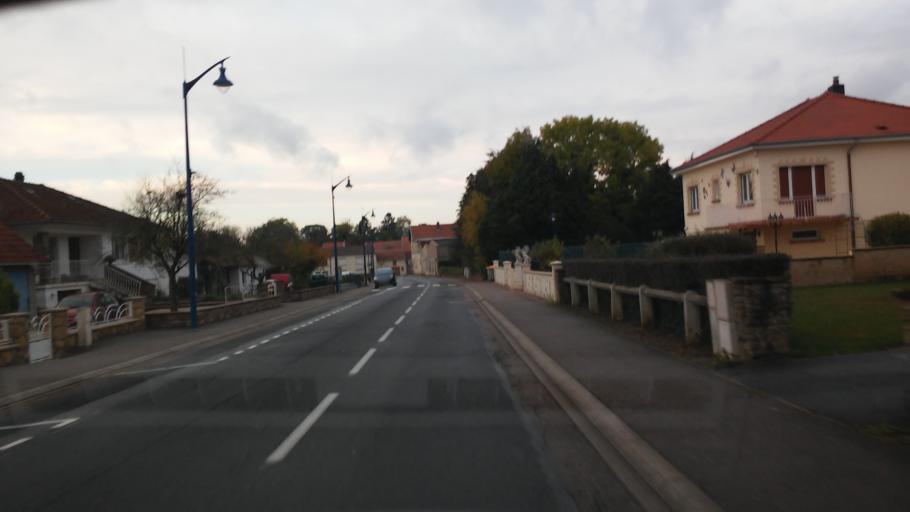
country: FR
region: Lorraine
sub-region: Departement de la Moselle
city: Ennery
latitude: 49.2241
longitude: 6.2196
